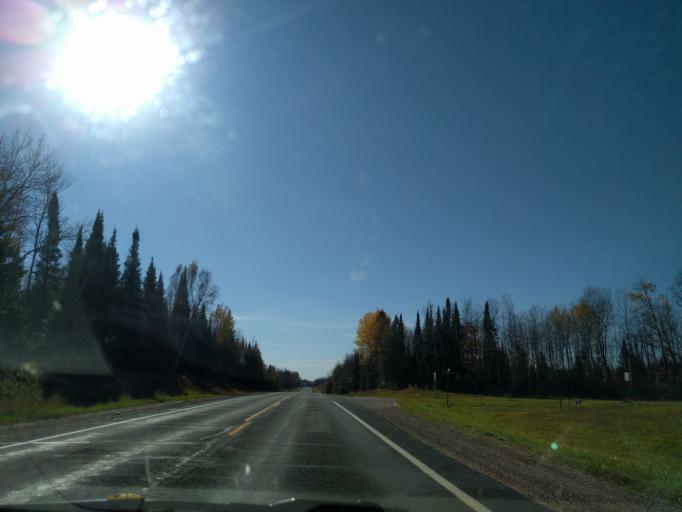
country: US
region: Michigan
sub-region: Iron County
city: Crystal Falls
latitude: 46.1875
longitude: -88.0345
